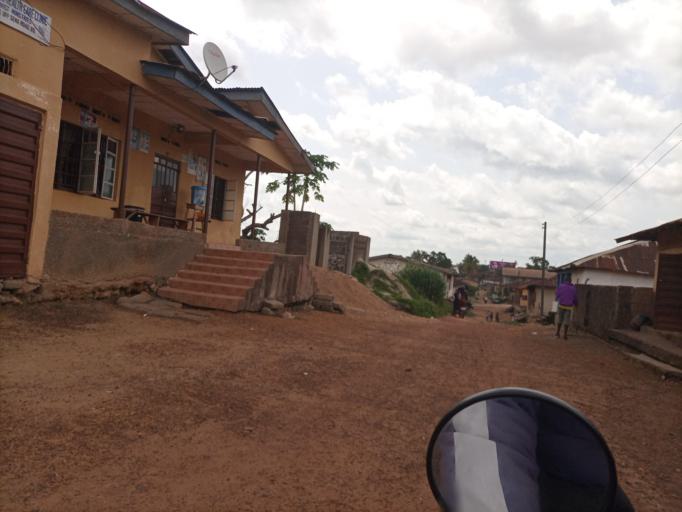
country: SL
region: Southern Province
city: Bo
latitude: 7.9520
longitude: -11.7320
